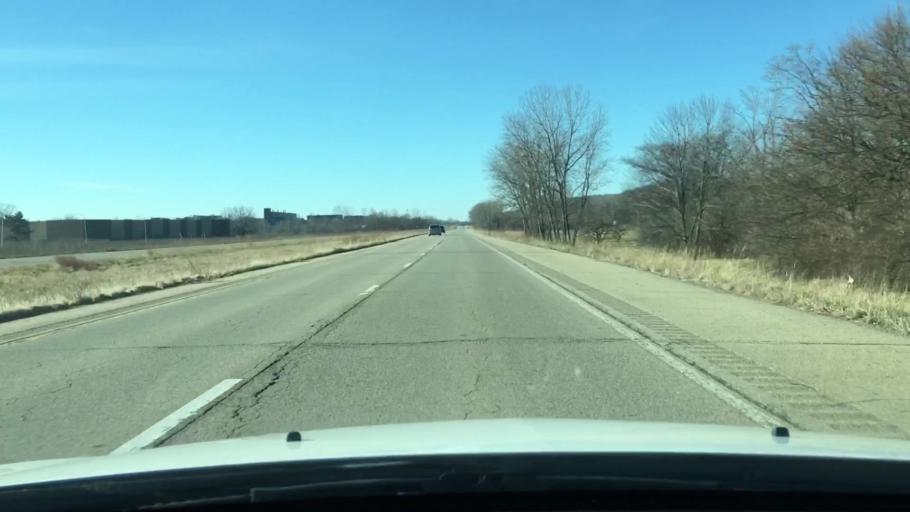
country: US
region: Illinois
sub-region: Peoria County
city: Glasford
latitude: 40.5650
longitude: -89.7336
